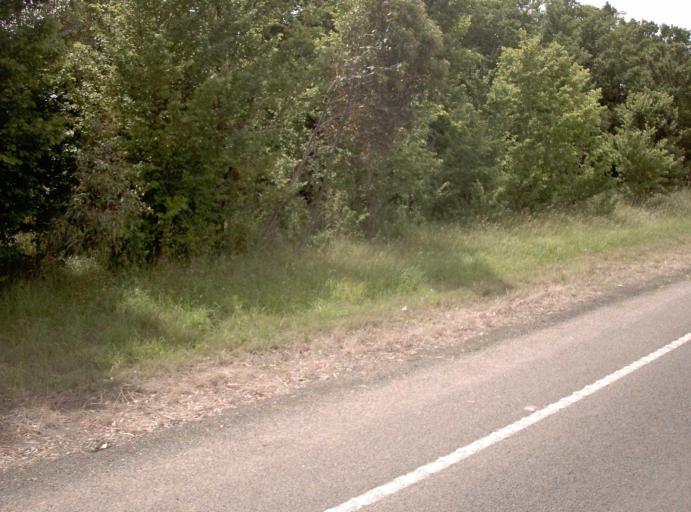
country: AU
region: Victoria
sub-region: Wellington
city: Sale
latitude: -38.0798
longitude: 147.0500
